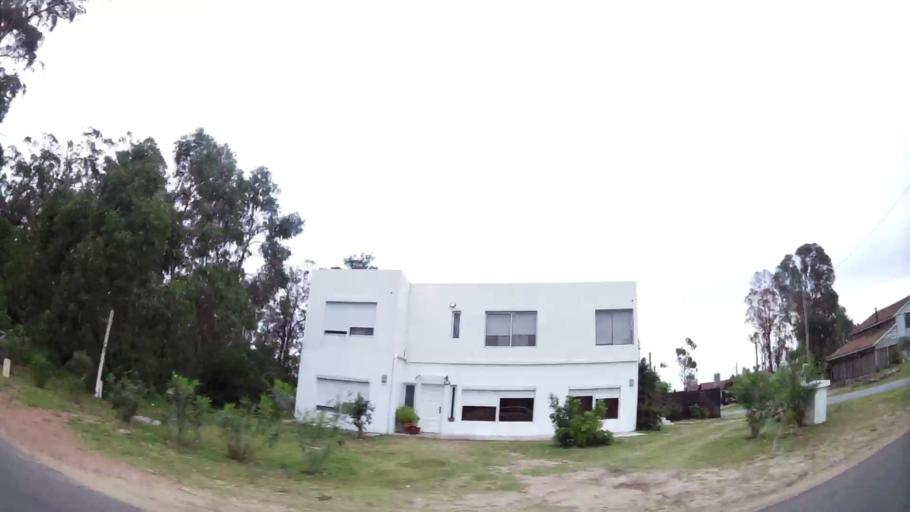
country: UY
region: Maldonado
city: Maldonado
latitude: -34.9028
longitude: -54.9991
